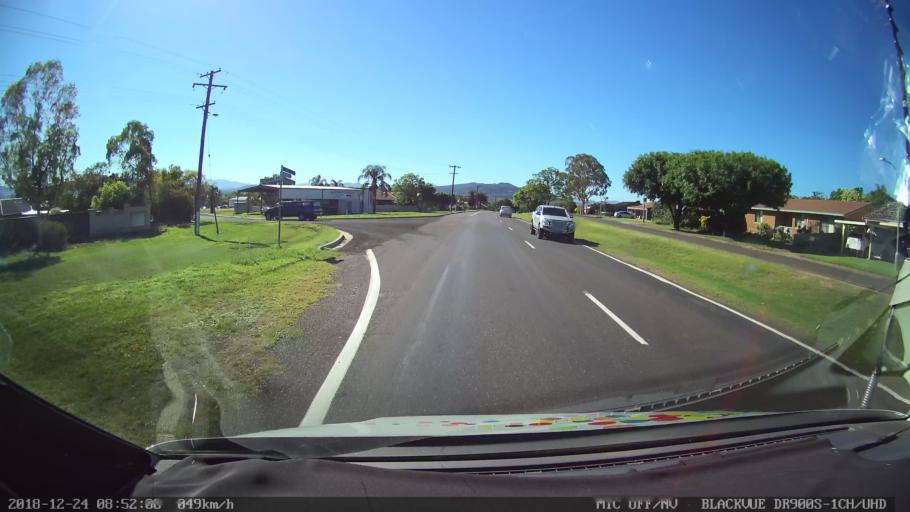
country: AU
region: New South Wales
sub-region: Liverpool Plains
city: Quirindi
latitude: -31.4897
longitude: 150.6779
